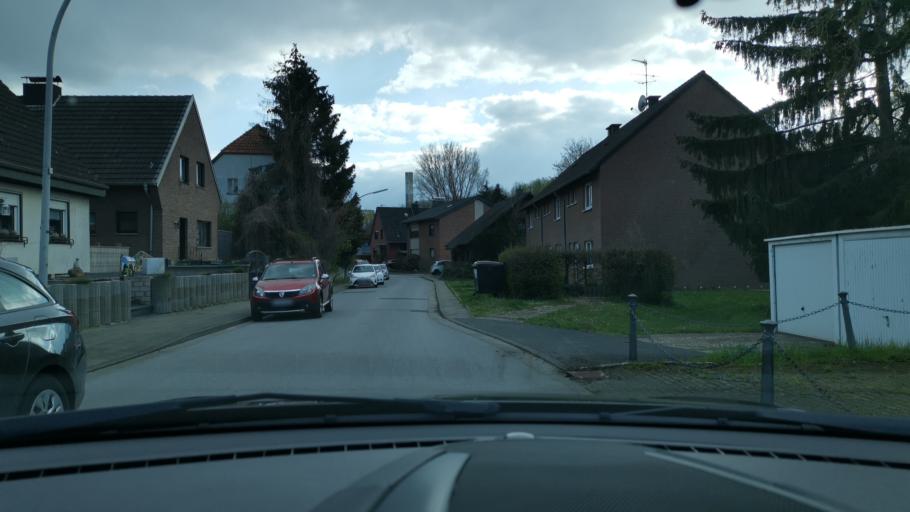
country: DE
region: North Rhine-Westphalia
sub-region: Regierungsbezirk Dusseldorf
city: Grevenbroich
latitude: 51.0726
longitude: 6.5889
